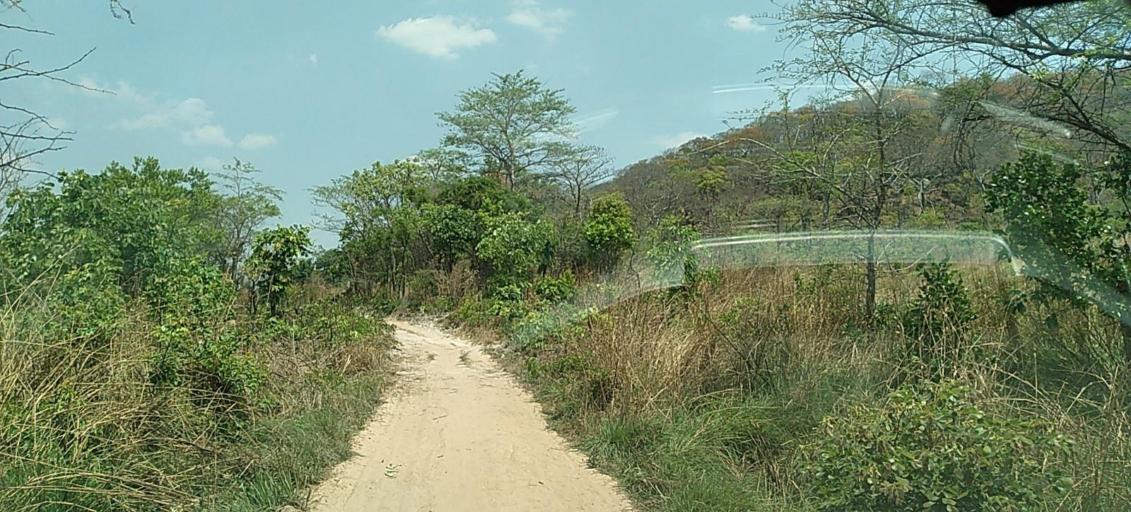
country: ZM
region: North-Western
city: Kasempa
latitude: -13.5280
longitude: 25.8223
